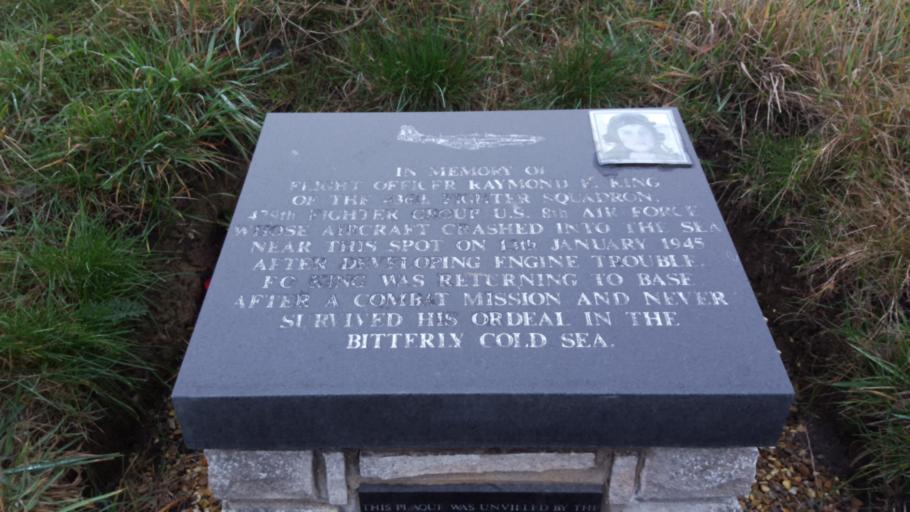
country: GB
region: England
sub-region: Essex
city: Clacton-on-Sea
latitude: 51.7933
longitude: 1.1693
